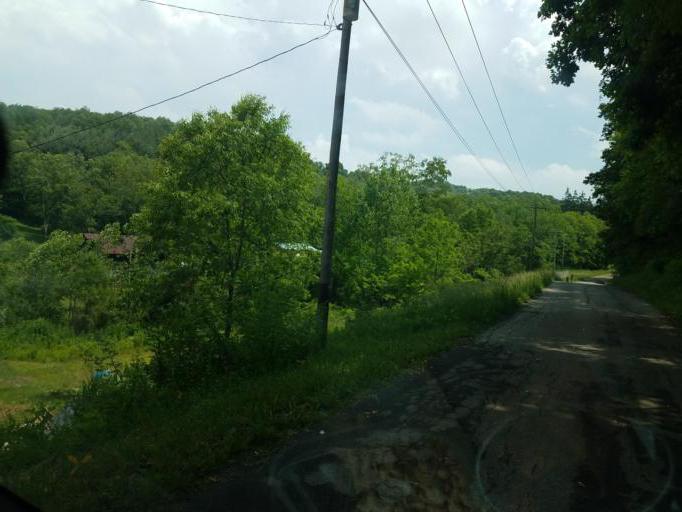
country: US
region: Ohio
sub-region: Knox County
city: Oak Hill
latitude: 40.3517
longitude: -82.2418
